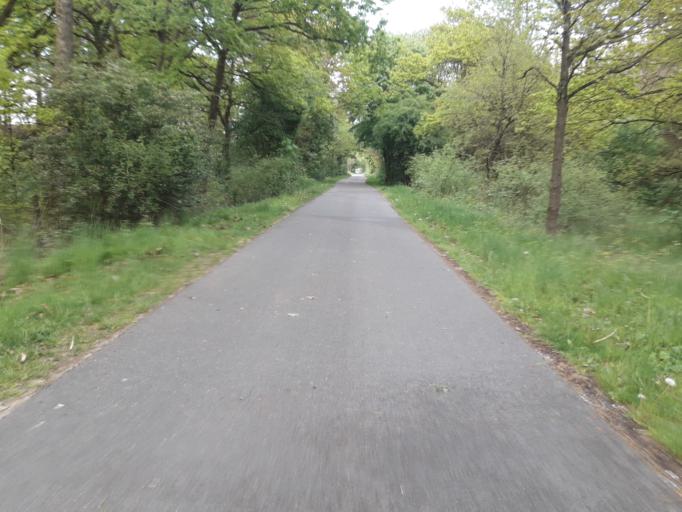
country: DE
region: North Rhine-Westphalia
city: Bad Lippspringe
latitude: 51.7749
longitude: 8.7961
